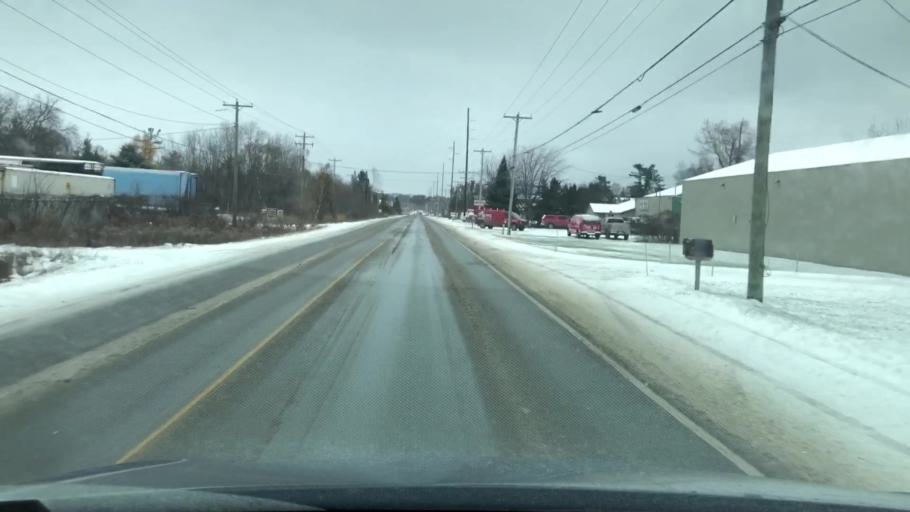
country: US
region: Michigan
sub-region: Grand Traverse County
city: Traverse City
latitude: 44.7185
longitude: -85.6258
